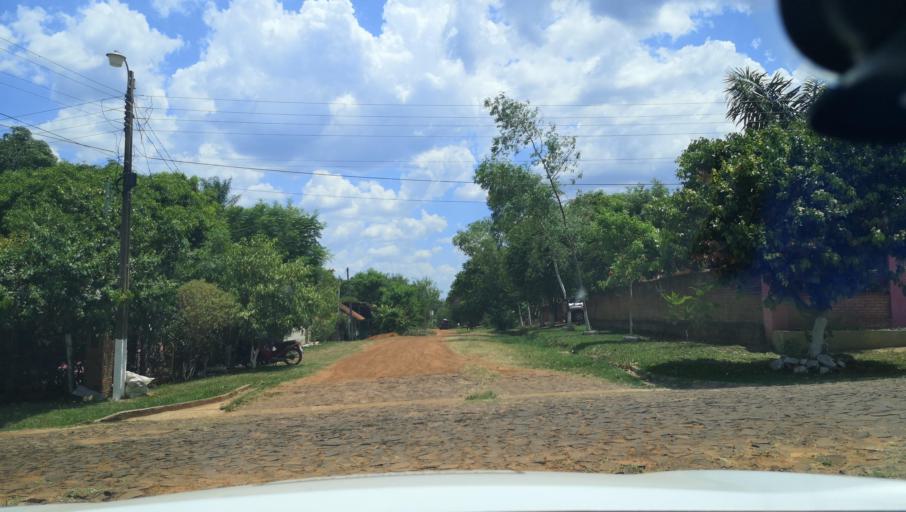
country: PY
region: Itapua
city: Carmen del Parana
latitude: -27.1703
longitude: -56.2449
